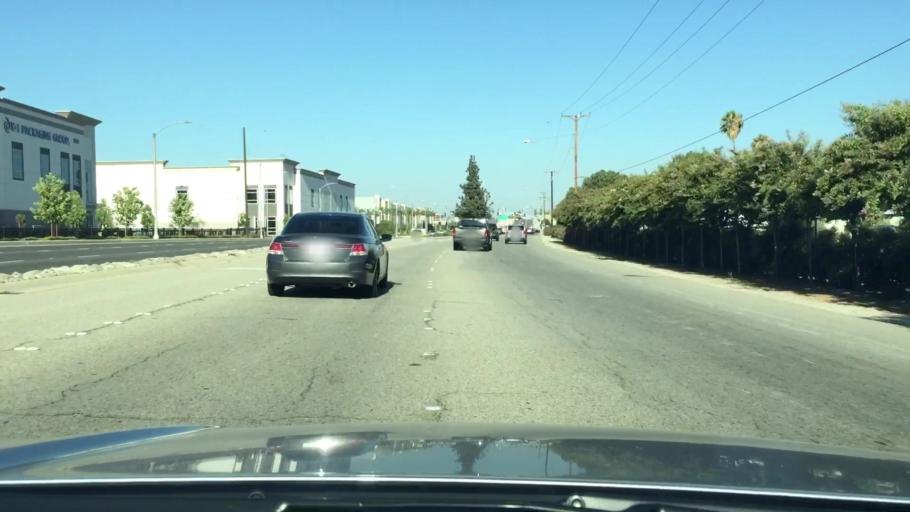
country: US
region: California
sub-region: Los Angeles County
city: Diamond Bar
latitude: 34.0524
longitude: -117.7890
